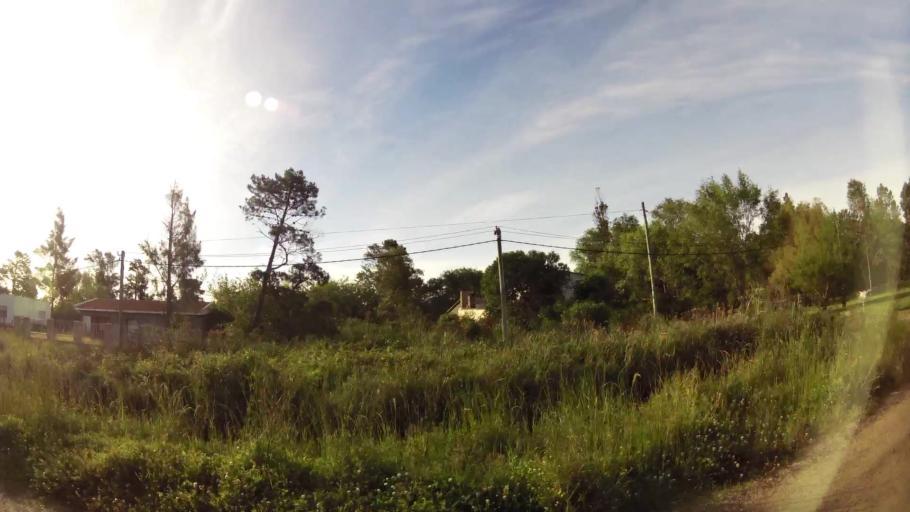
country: UY
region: Canelones
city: Empalme Olmos
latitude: -34.7906
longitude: -55.8583
